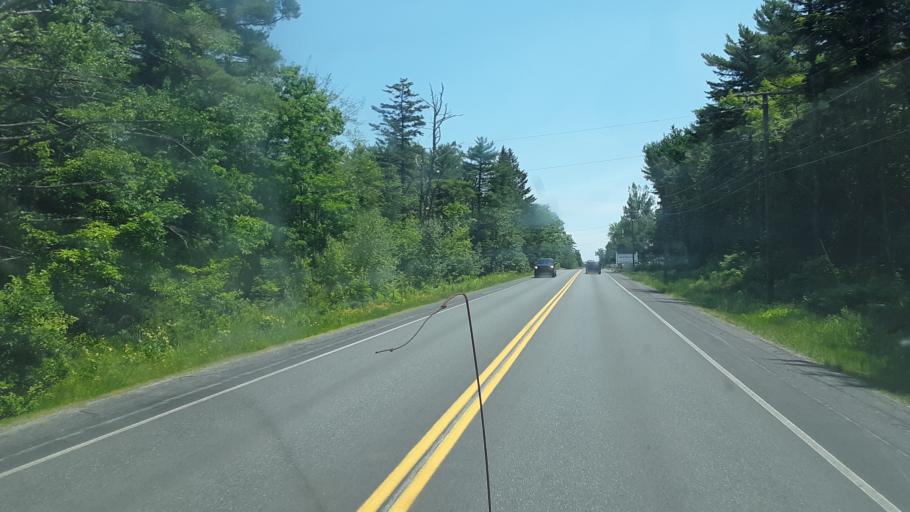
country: US
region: Maine
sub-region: Hancock County
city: Hancock
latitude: 44.5273
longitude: -68.2495
